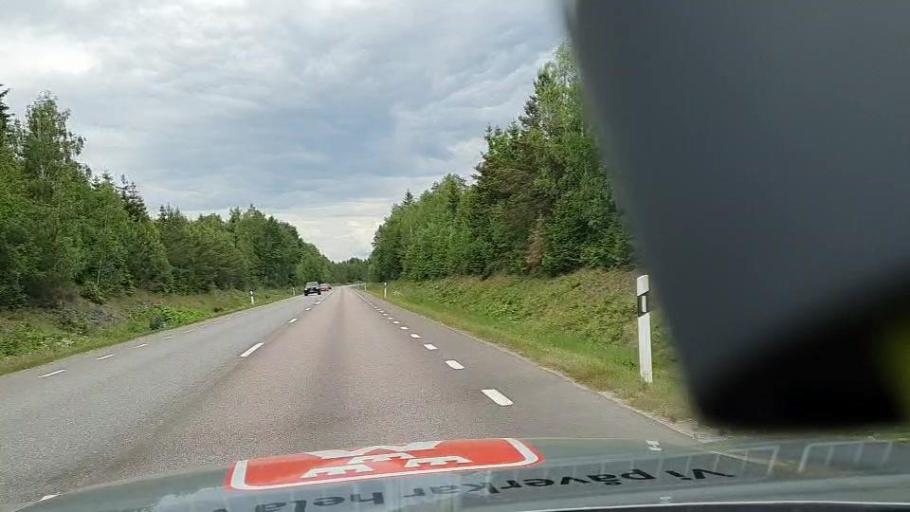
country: SE
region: Kalmar
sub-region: Emmaboda Kommun
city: Emmaboda
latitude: 56.4476
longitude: 15.5625
